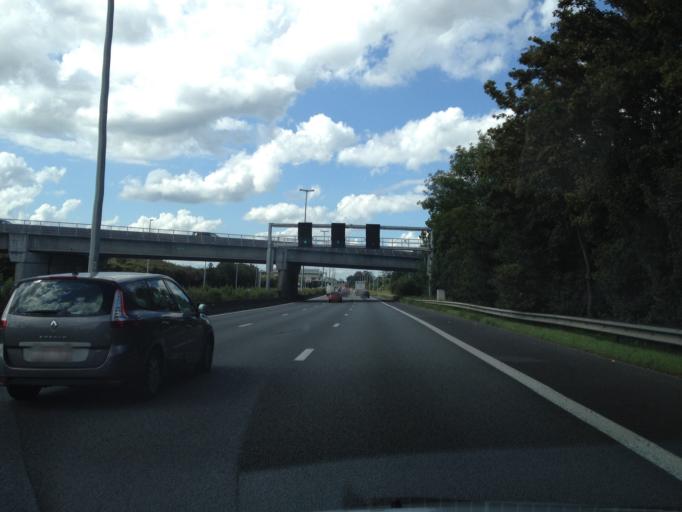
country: BE
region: Flanders
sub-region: Provincie Oost-Vlaanderen
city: Merelbeke
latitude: 50.9996
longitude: 3.7696
